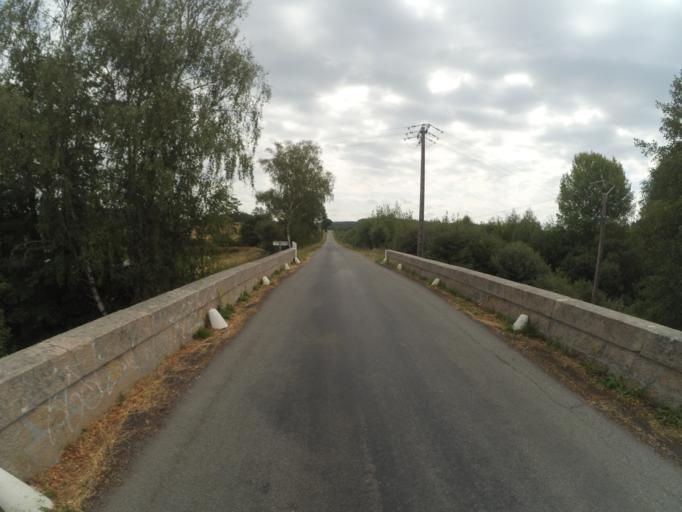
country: FR
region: Limousin
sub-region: Departement de la Creuse
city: La Courtine
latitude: 45.6657
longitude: 2.1785
